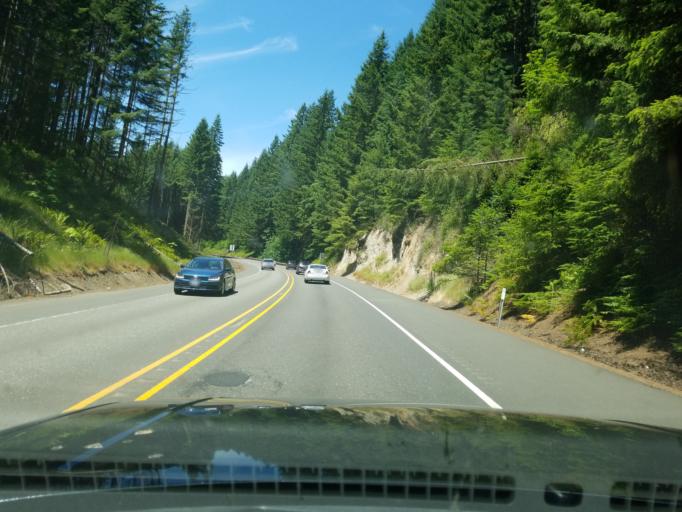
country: US
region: Oregon
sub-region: Washington County
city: Banks
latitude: 45.7029
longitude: -123.2217
